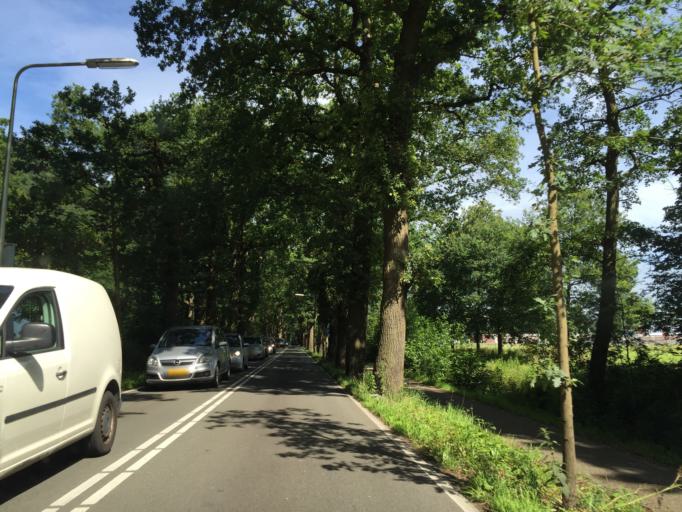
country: NL
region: South Holland
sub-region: Gemeente Wassenaar
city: Wassenaar
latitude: 52.1492
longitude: 4.3902
